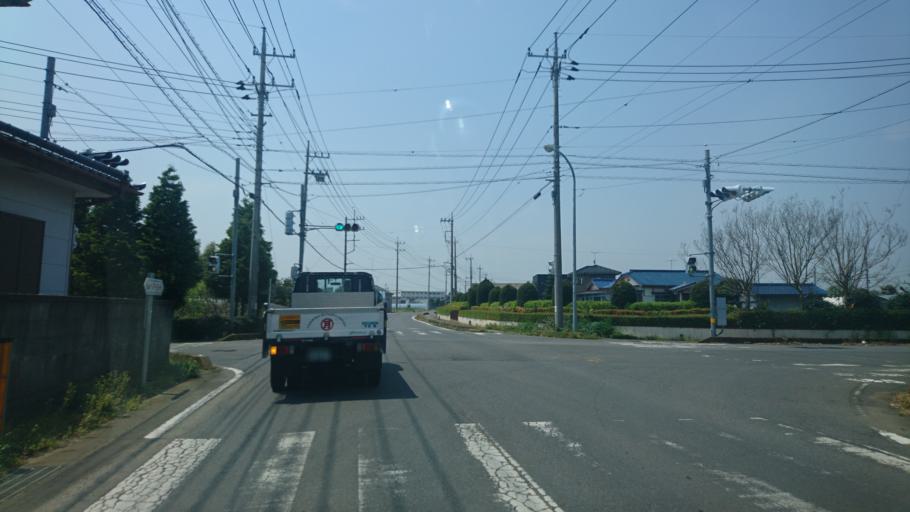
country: JP
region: Ibaraki
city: Shimodate
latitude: 36.2514
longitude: 139.9395
